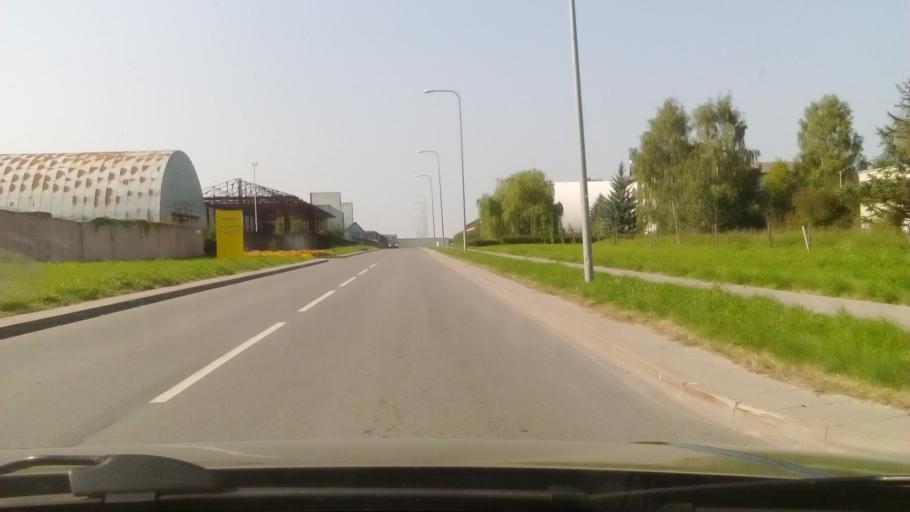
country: LT
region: Alytaus apskritis
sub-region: Alytus
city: Alytus
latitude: 54.4258
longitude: 24.0299
